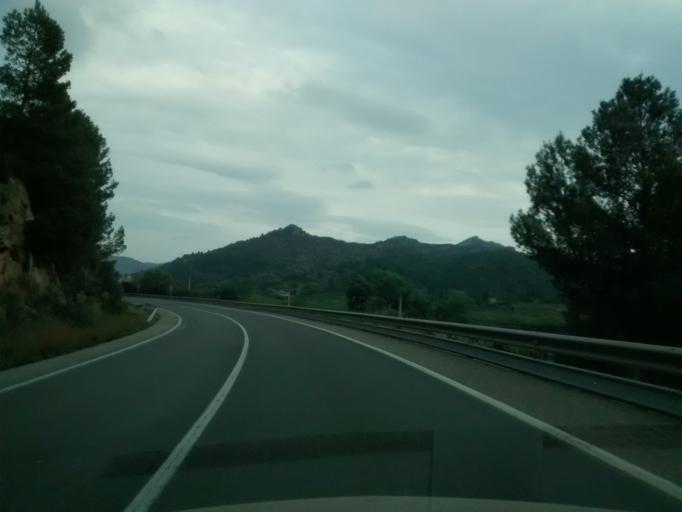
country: ES
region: Catalonia
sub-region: Provincia de Tarragona
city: Benifallet
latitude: 40.9599
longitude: 0.5079
